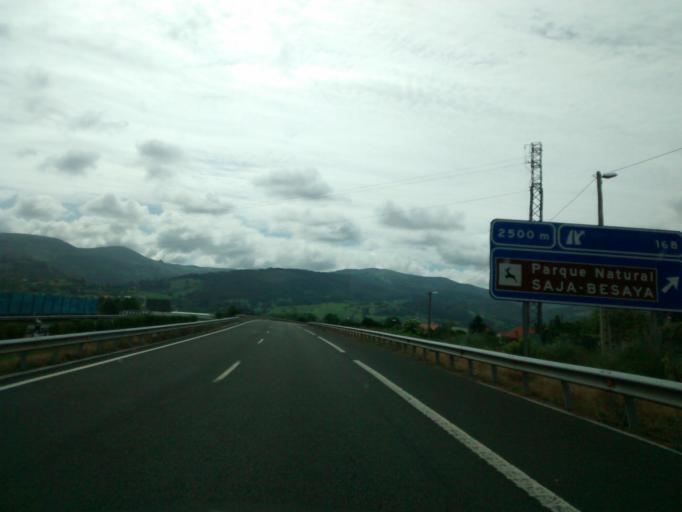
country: ES
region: Cantabria
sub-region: Provincia de Cantabria
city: Los Corrales de Buelna
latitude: 43.2761
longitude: -4.0790
